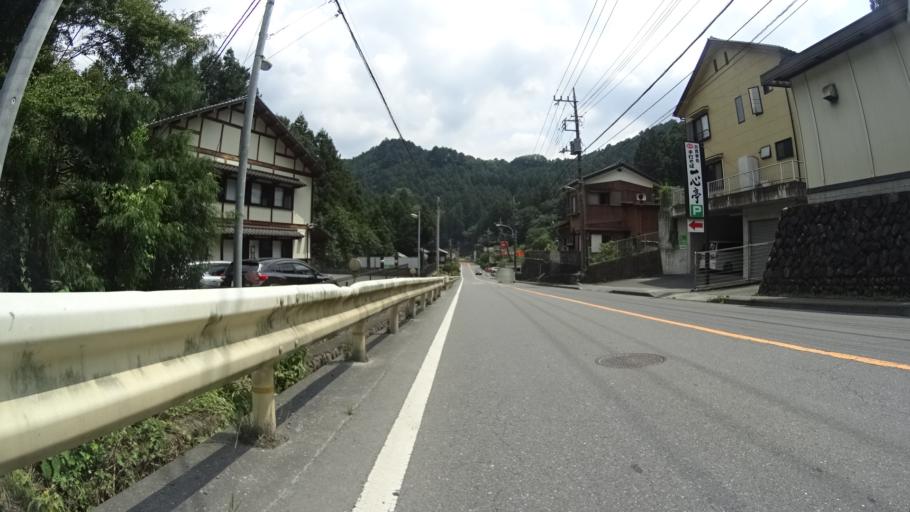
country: JP
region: Tokyo
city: Ome
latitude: 35.8077
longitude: 139.1590
